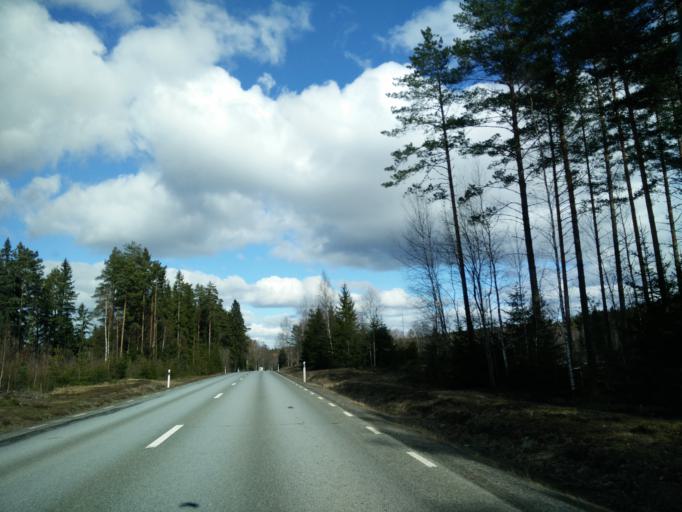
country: SE
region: Vaermland
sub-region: Hagfors Kommun
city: Hagfors
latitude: 59.9804
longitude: 13.5717
